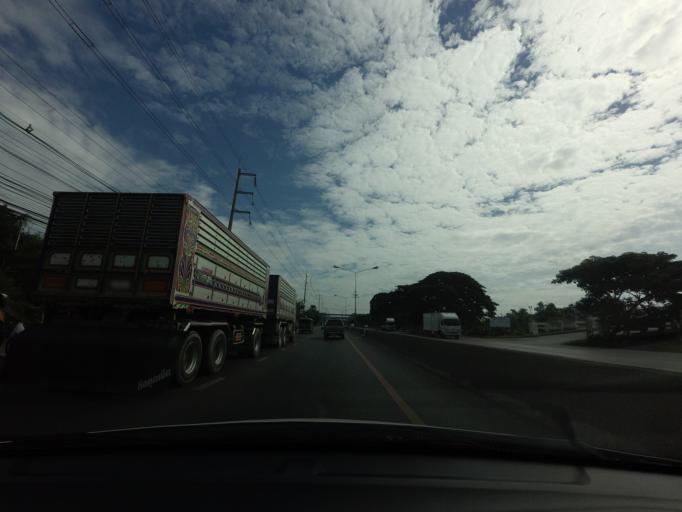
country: TH
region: Pathum Thani
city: Ban Rangsit
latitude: 14.0357
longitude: 100.7744
